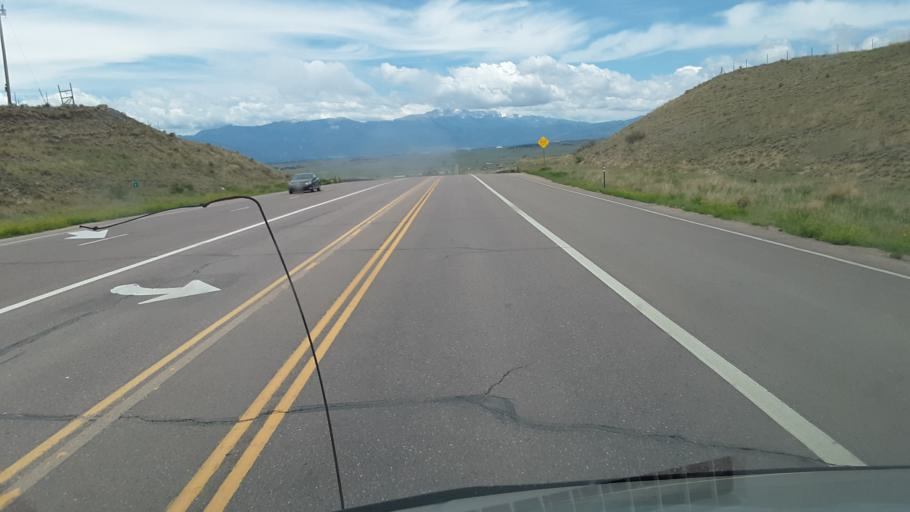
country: US
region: Colorado
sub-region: El Paso County
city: Cimarron Hills
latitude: 38.8385
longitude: -104.5731
